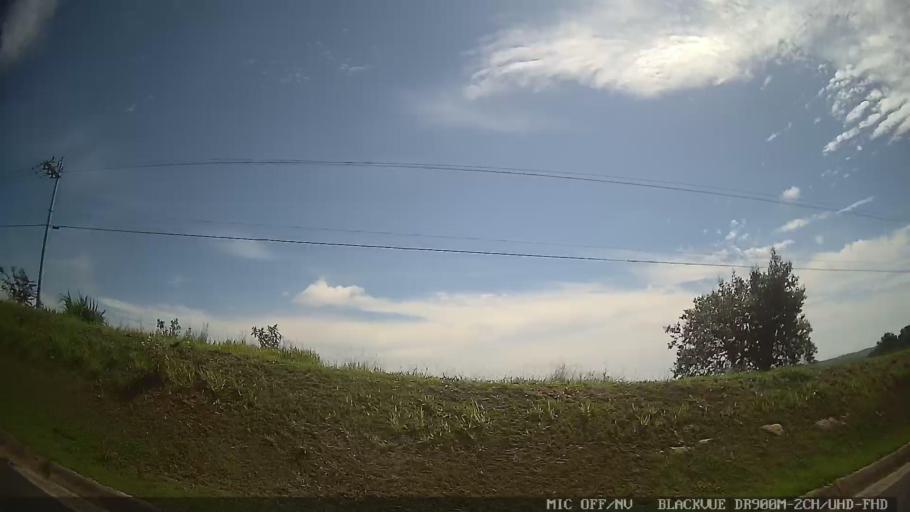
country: BR
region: Sao Paulo
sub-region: Porto Feliz
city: Porto Feliz
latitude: -23.2064
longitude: -47.5984
